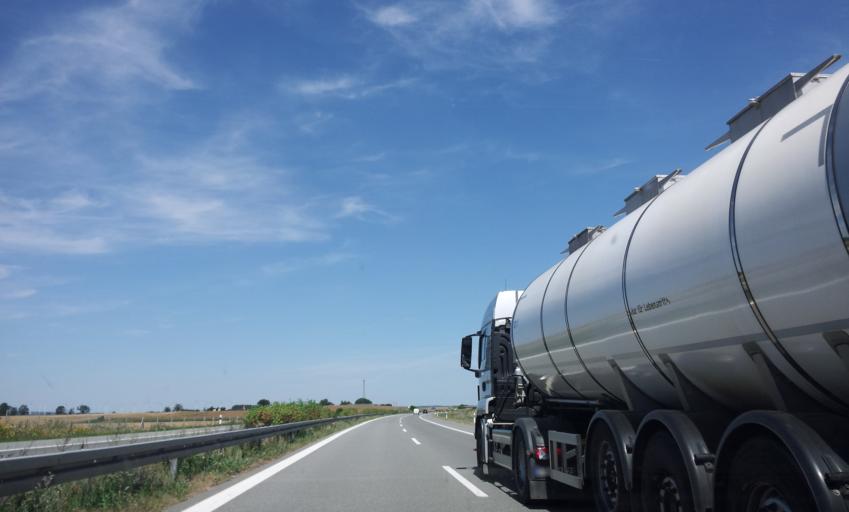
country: DE
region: Mecklenburg-Vorpommern
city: Neuenkirchen
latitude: 53.6270
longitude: 13.3667
